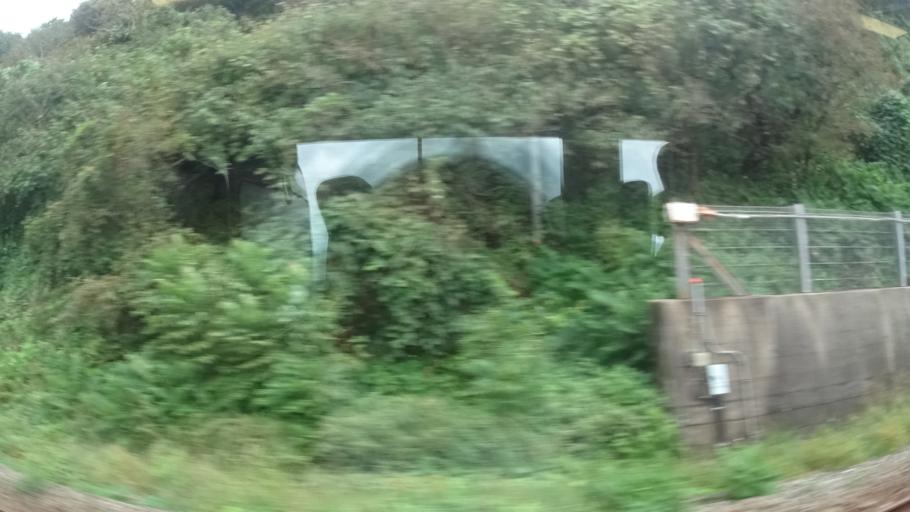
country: JP
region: Niigata
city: Murakami
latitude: 38.4631
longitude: 139.4995
